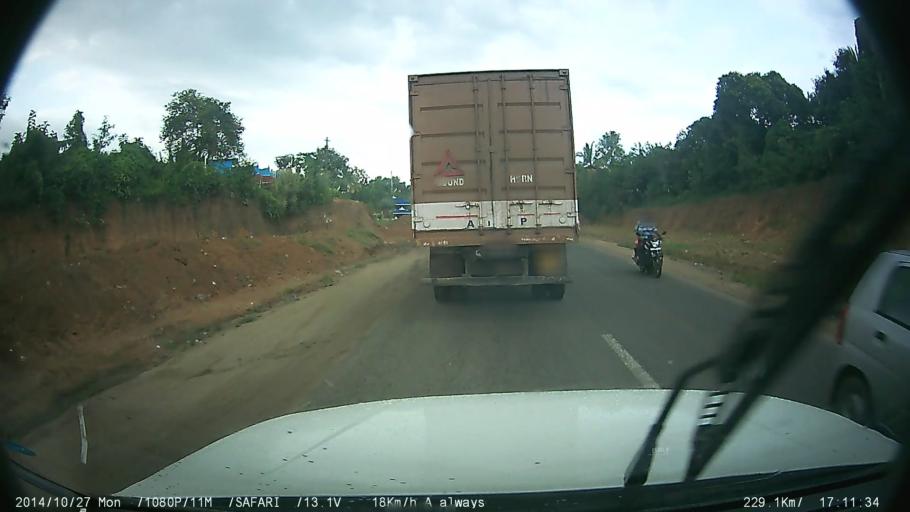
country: IN
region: Kerala
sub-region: Thrissur District
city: Chelakara
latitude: 10.6079
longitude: 76.4956
